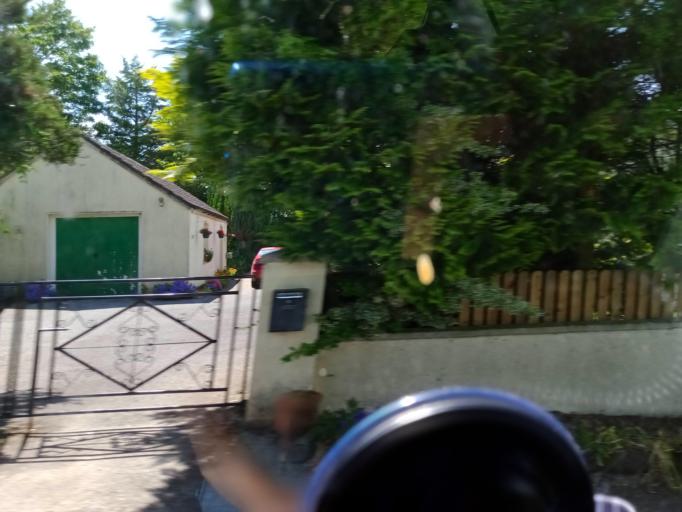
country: IE
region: Leinster
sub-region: Kilkenny
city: Thomastown
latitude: 52.5550
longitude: -7.0999
